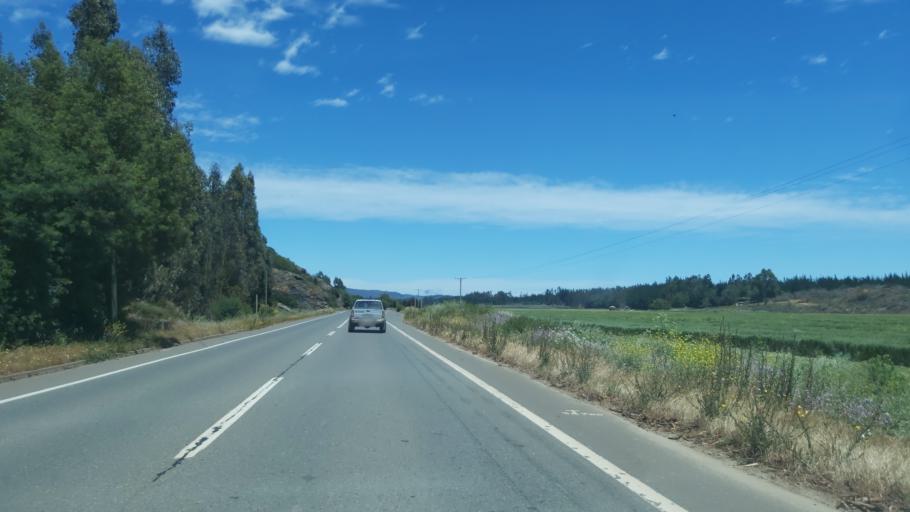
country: CL
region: Maule
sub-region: Provincia de Talca
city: Constitucion
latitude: -35.2846
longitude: -72.3622
